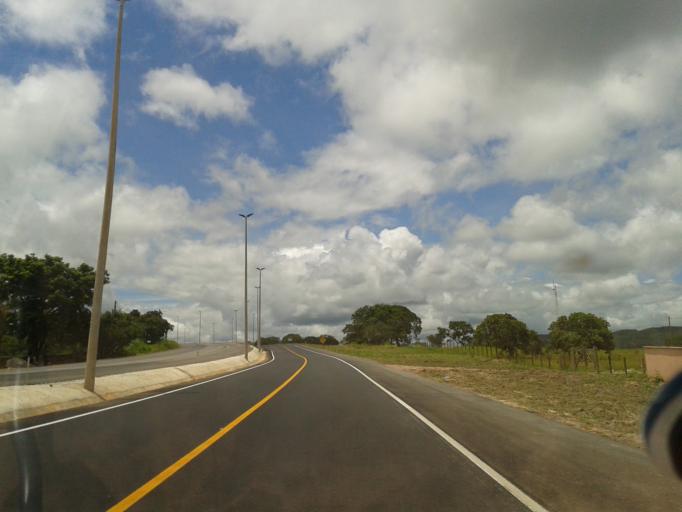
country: BR
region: Goias
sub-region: Goias
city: Goias
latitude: -15.9843
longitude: -50.0800
